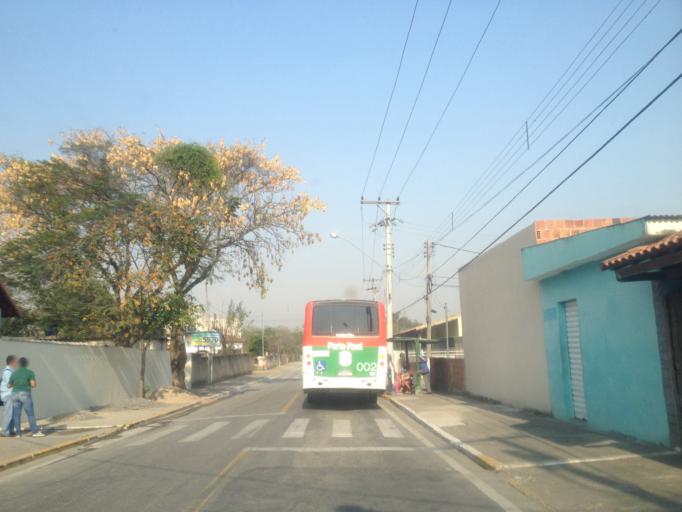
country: BR
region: Rio de Janeiro
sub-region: Porto Real
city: Porto Real
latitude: -22.4641
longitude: -44.3558
